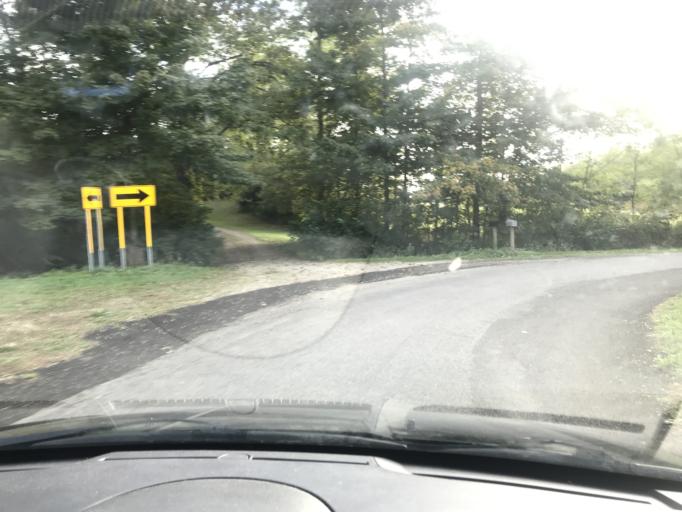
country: US
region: Ohio
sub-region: Logan County
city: West Liberty
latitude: 40.2251
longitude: -83.6691
